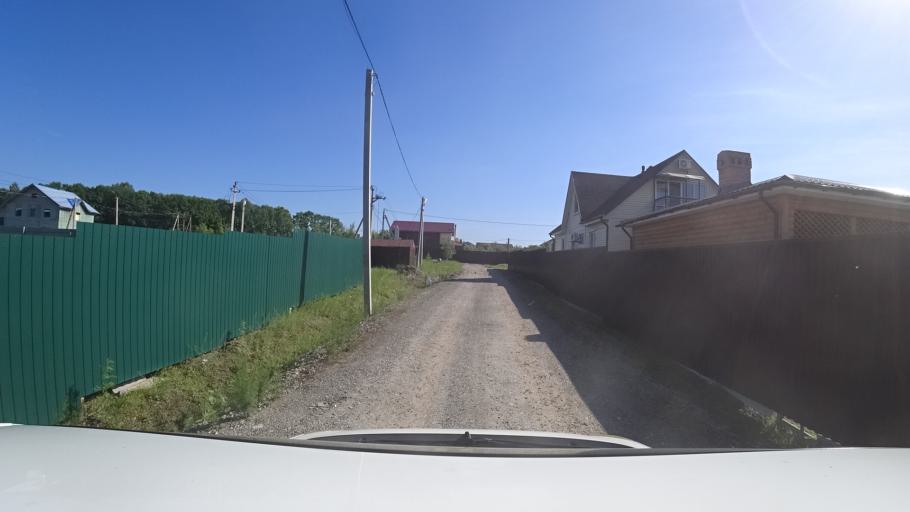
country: RU
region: Khabarovsk Krai
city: Topolevo
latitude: 48.5497
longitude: 135.1825
